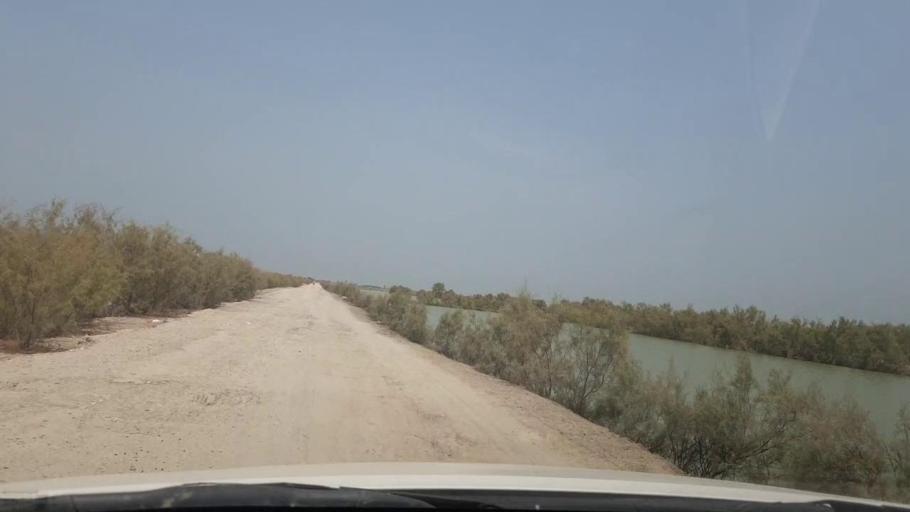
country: PK
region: Sindh
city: Rustam jo Goth
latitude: 28.0611
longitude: 68.8166
